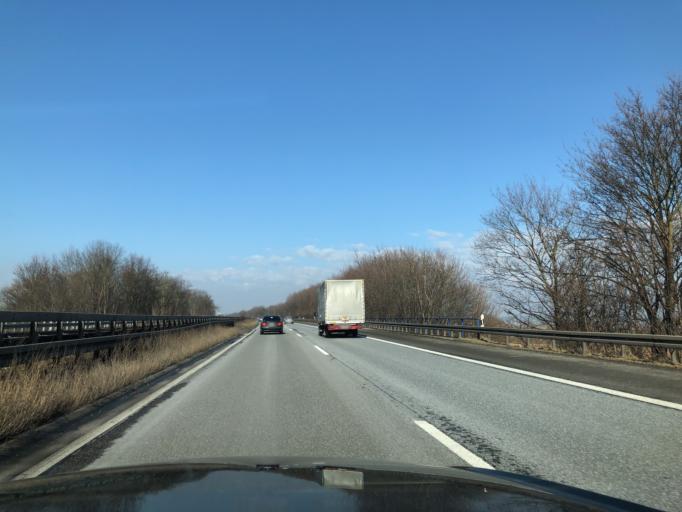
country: DE
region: North Rhine-Westphalia
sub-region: Regierungsbezirk Koln
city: Rheinbach
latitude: 50.6259
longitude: 6.9742
